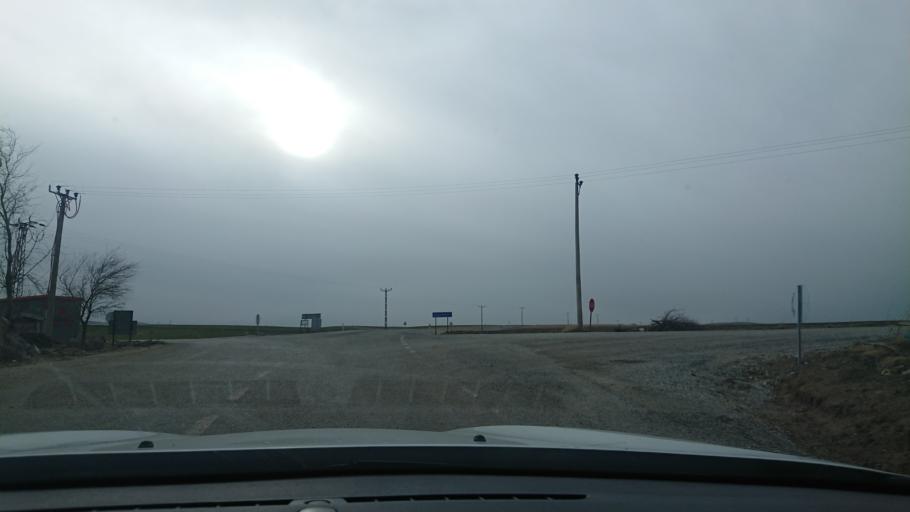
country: TR
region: Aksaray
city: Agacoren
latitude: 38.9246
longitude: 33.9486
